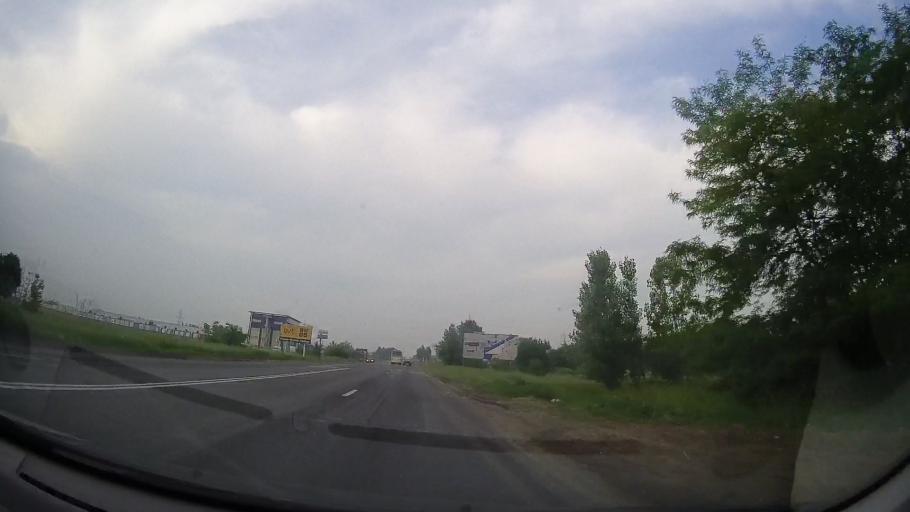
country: RO
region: Timis
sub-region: Comuna Giroc
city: Chisoda
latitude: 45.7088
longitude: 21.1889
